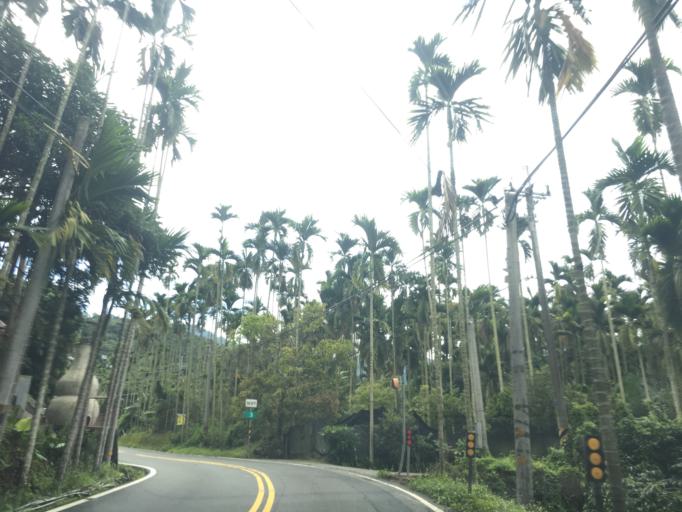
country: TW
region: Taiwan
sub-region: Yunlin
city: Douliu
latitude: 23.5672
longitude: 120.5714
